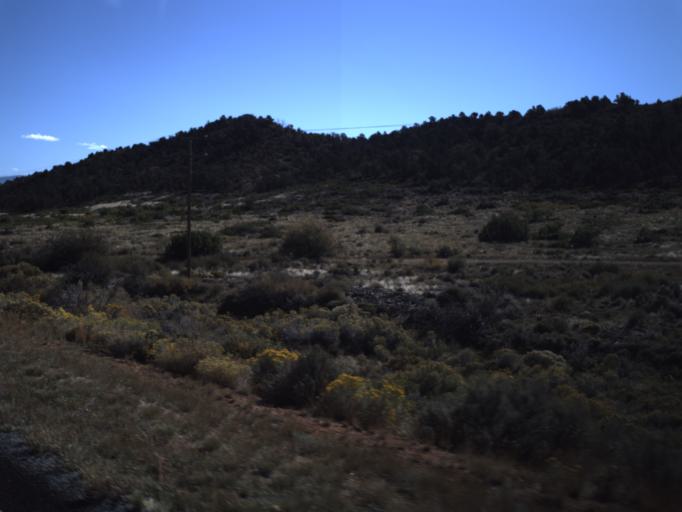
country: US
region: Utah
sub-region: Iron County
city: Cedar City
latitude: 37.6156
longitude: -113.3366
